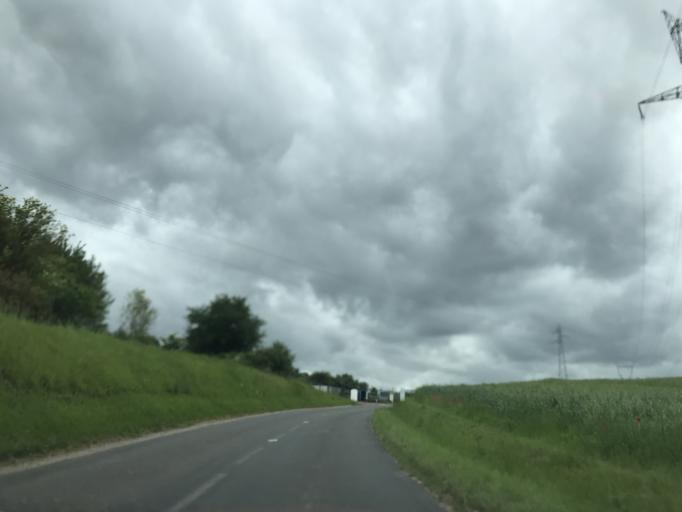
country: FR
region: Haute-Normandie
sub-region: Departement de l'Eure
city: Garennes-sur-Eure
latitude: 48.8965
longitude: 1.4269
